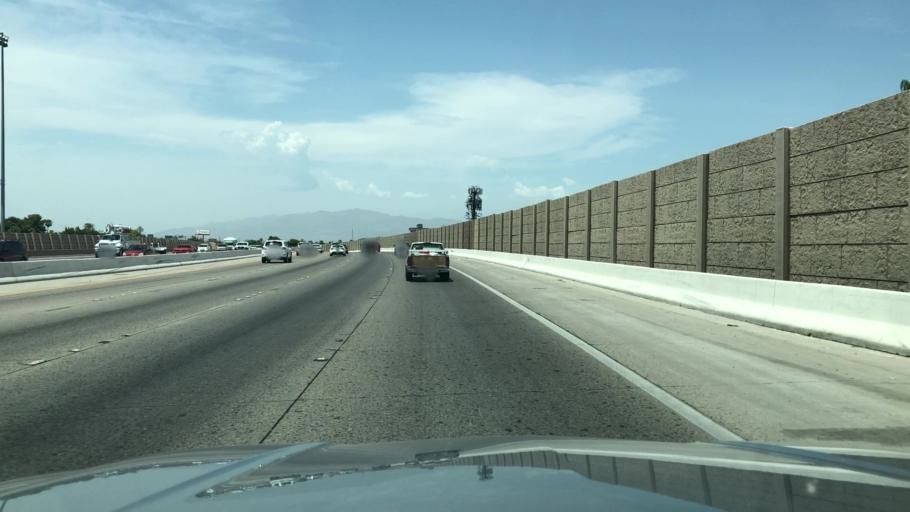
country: US
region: Nevada
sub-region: Clark County
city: Winchester
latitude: 36.1208
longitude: -115.0828
